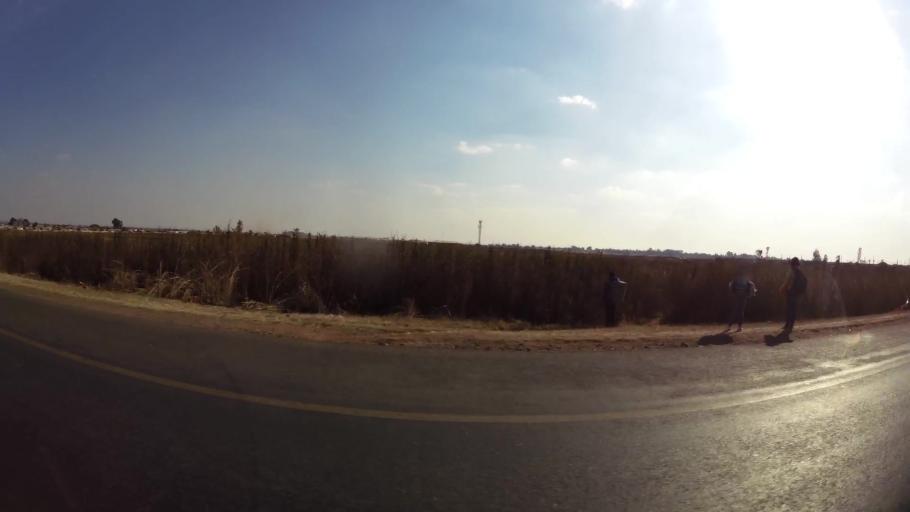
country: ZA
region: Gauteng
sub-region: Ekurhuleni Metropolitan Municipality
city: Benoni
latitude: -26.1578
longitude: 28.3971
